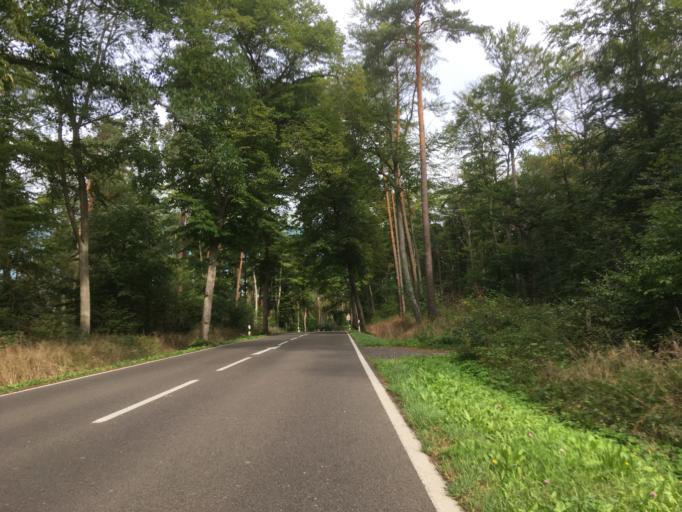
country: DE
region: Brandenburg
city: Templin
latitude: 53.1473
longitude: 13.5491
